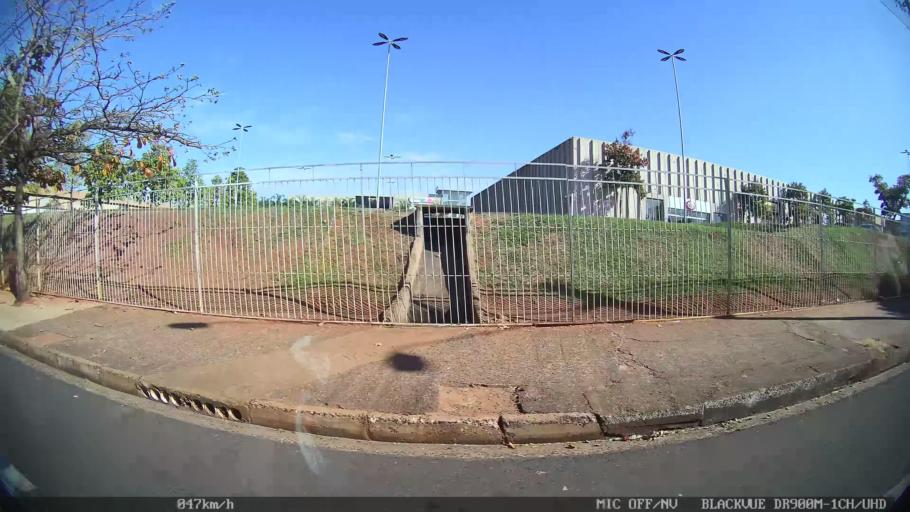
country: BR
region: Sao Paulo
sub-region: Sao Jose Do Rio Preto
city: Sao Jose do Rio Preto
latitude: -20.7710
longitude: -49.3853
